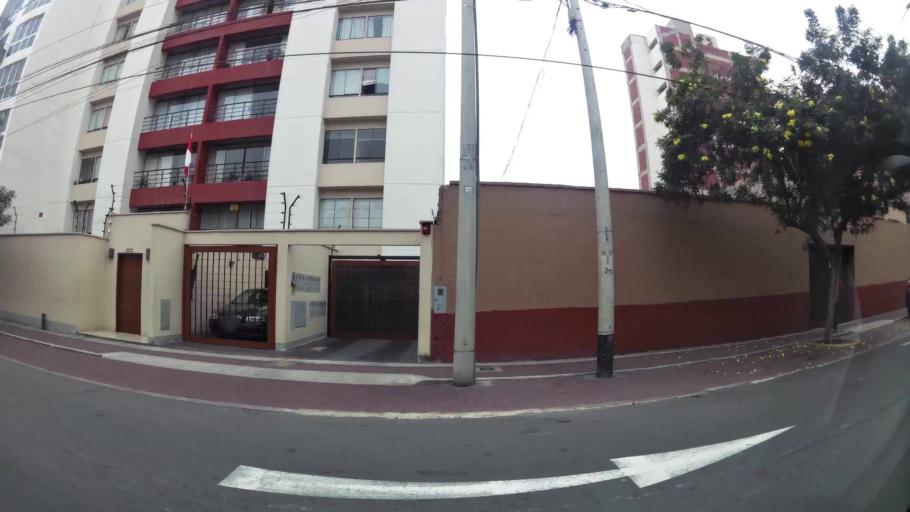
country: PE
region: Lima
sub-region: Lima
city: San Isidro
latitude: -12.1206
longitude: -77.0337
